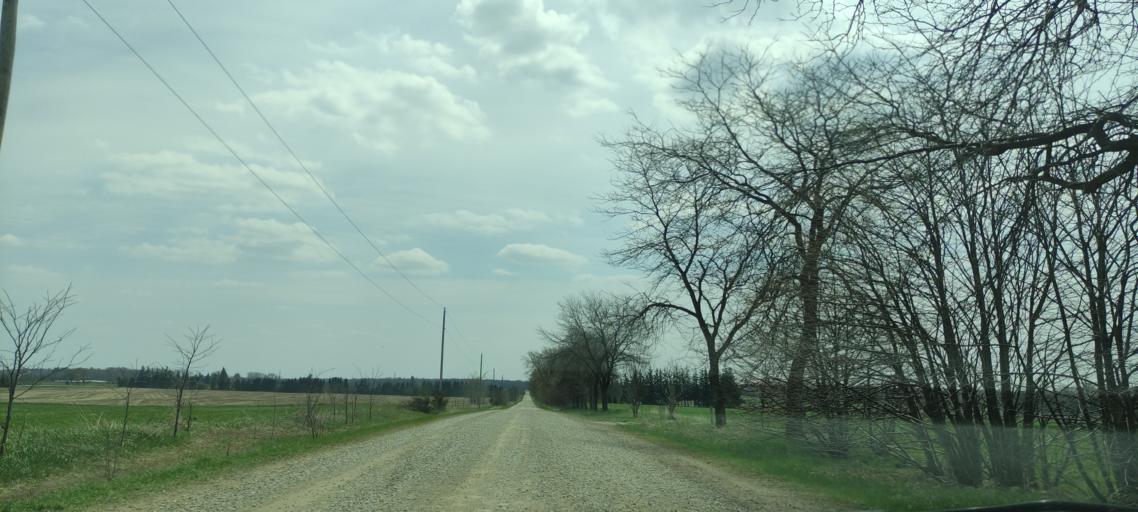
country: CA
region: Ontario
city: Stratford
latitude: 43.3446
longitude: -80.7427
